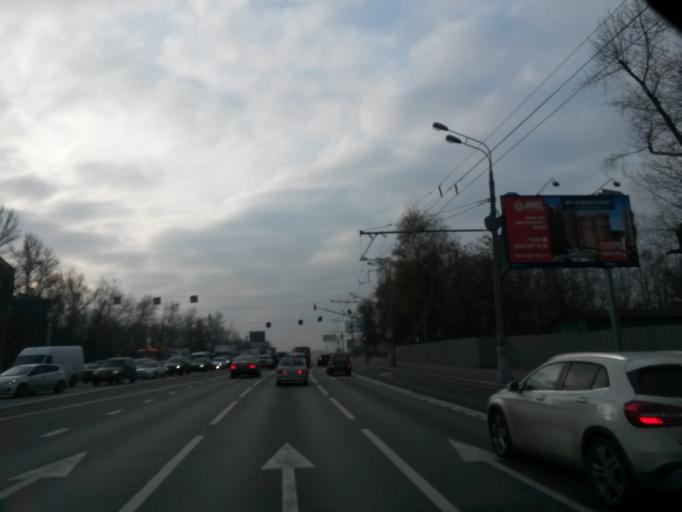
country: RU
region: Moscow
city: Nagornyy
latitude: 55.6704
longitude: 37.6256
